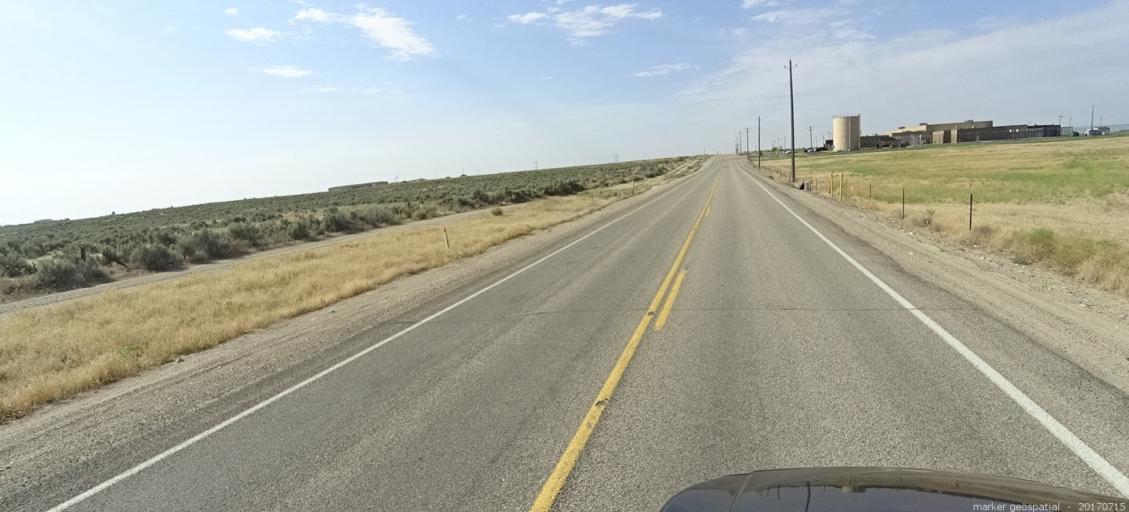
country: US
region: Idaho
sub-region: Ada County
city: Boise
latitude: 43.4645
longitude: -116.2344
